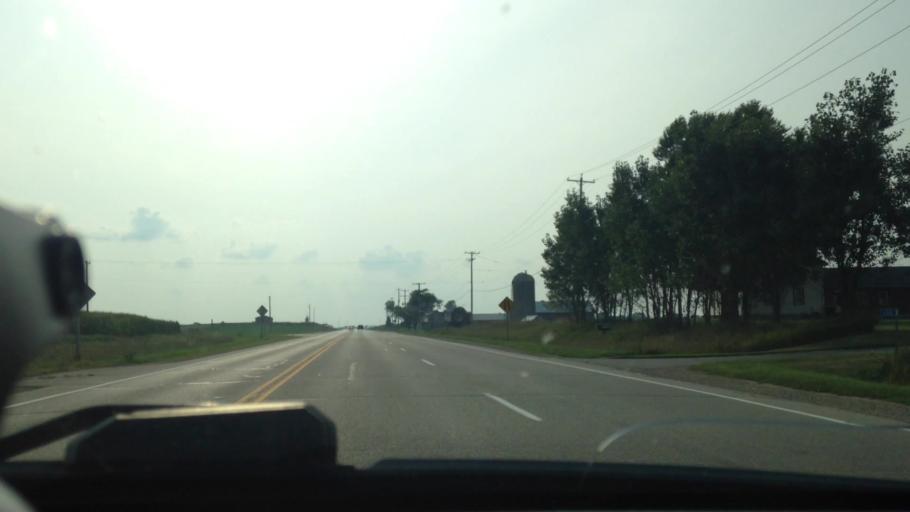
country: US
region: Wisconsin
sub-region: Washington County
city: Hartford
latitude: 43.4215
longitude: -88.3584
